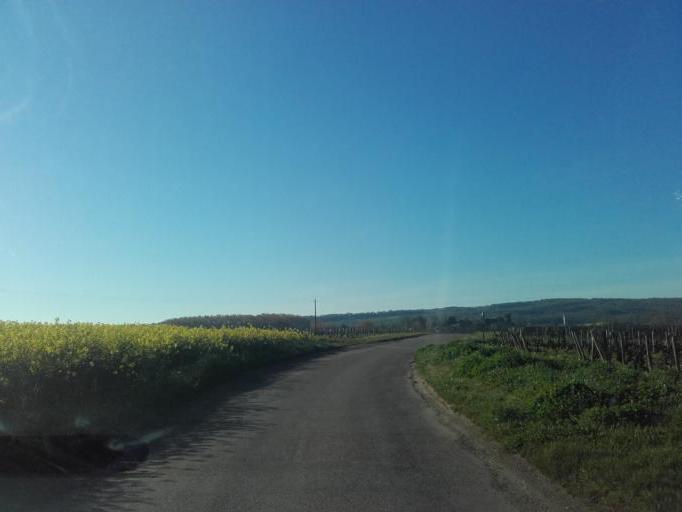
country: FR
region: Bourgogne
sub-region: Departement de Saone-et-Loire
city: Mellecey
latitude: 46.8179
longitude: 4.7260
